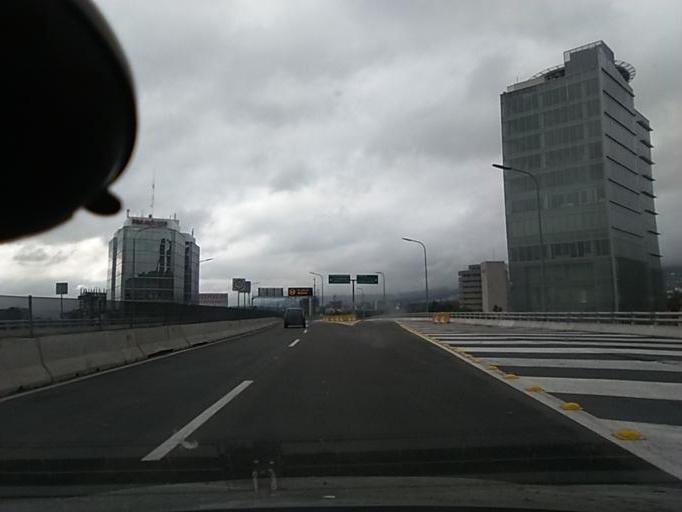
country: MX
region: Mexico City
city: Magdalena Contreras
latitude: 19.3118
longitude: -99.2197
